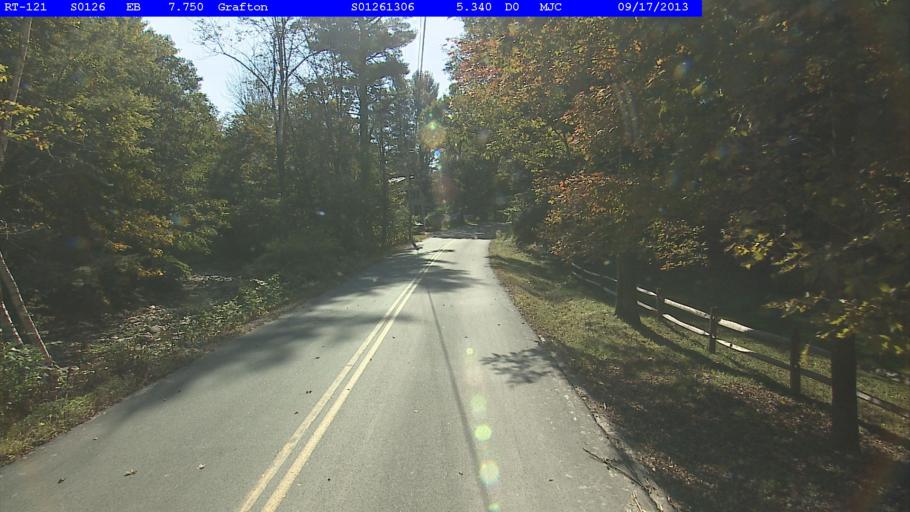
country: US
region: Vermont
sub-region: Windsor County
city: Chester
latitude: 43.1749
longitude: -72.6108
